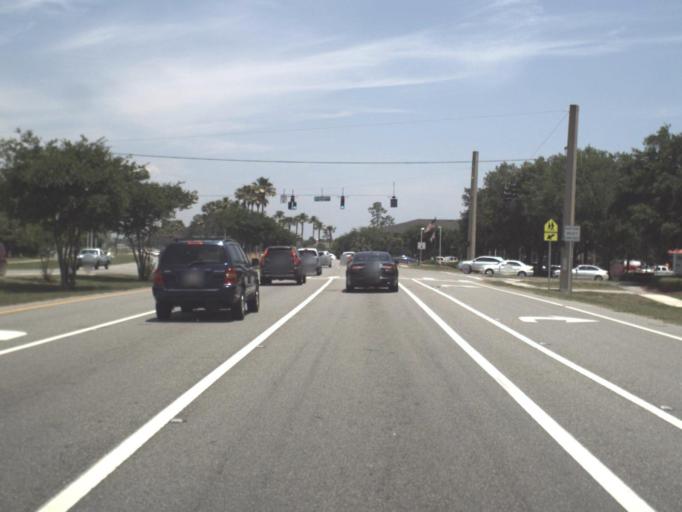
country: US
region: Florida
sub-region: Saint Johns County
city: Sawgrass
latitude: 30.2139
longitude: -81.3807
